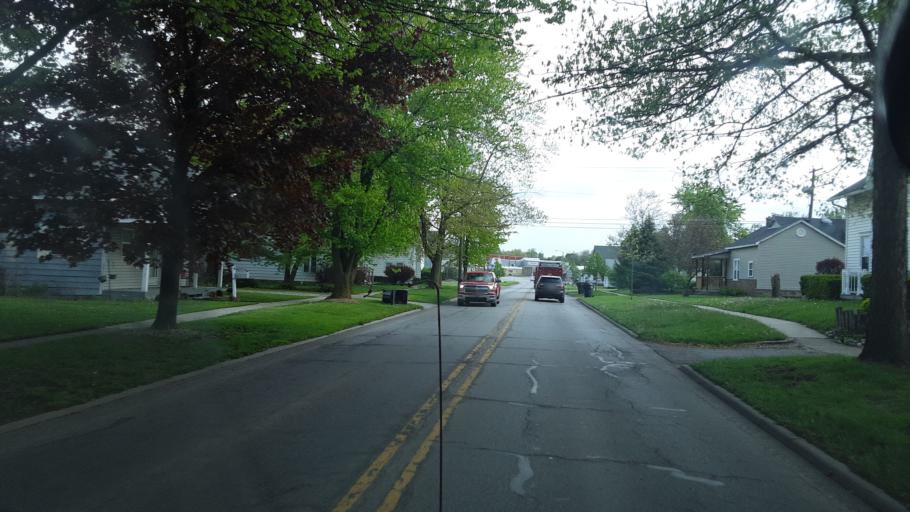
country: US
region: Indiana
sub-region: Whitley County
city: Churubusco
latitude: 41.2274
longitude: -85.3180
